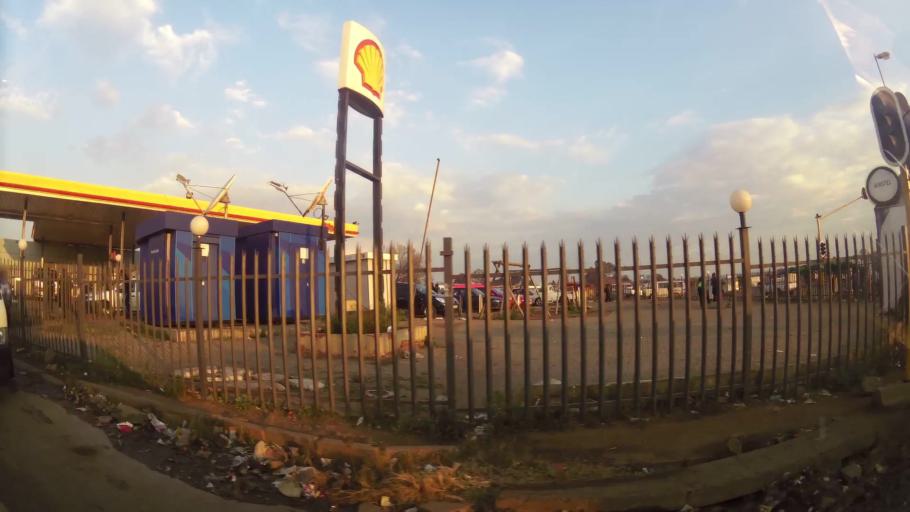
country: ZA
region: Gauteng
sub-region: City of Johannesburg Metropolitan Municipality
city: Orange Farm
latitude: -26.5355
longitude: 27.8839
